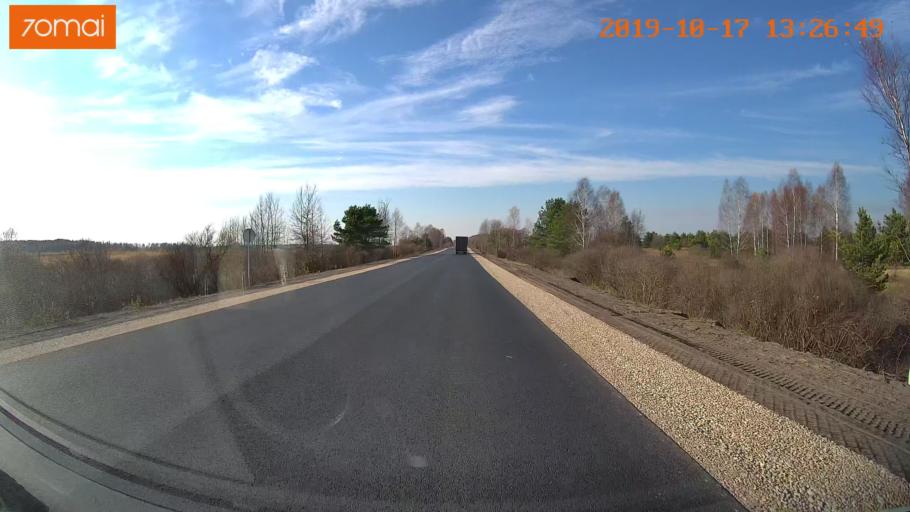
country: RU
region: Rjazan
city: Gus'-Zheleznyy
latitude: 55.1114
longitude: 40.9110
